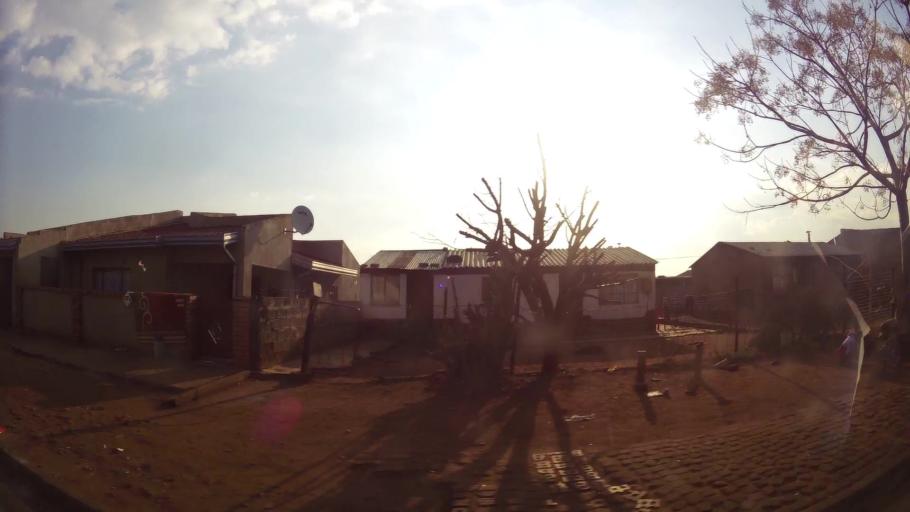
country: ZA
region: Gauteng
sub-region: Ekurhuleni Metropolitan Municipality
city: Germiston
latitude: -26.3513
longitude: 28.2076
